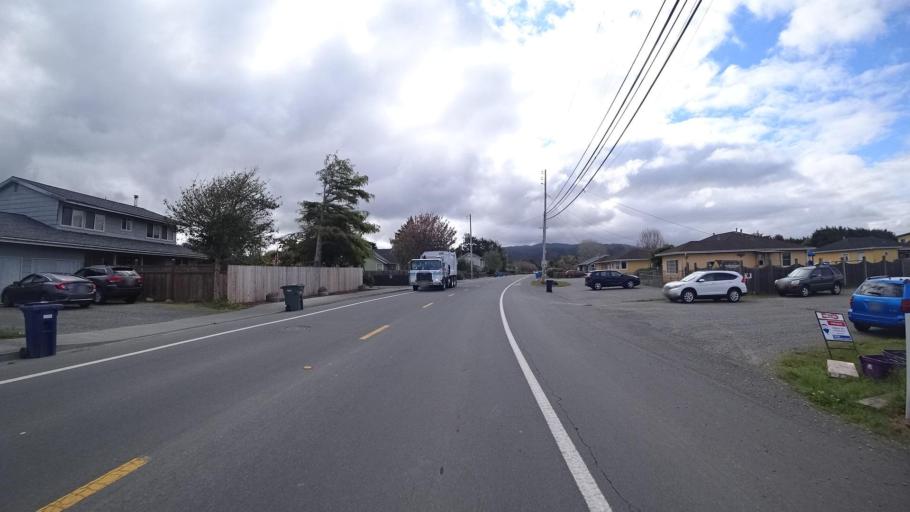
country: US
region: California
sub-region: Humboldt County
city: Arcata
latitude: 40.8924
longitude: -124.0924
